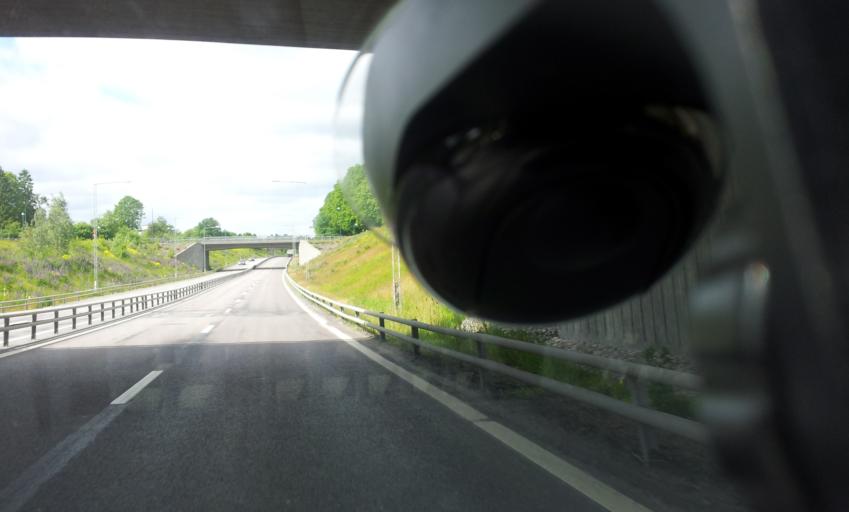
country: SE
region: OEstergoetland
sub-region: Norrkopings Kommun
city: Norrkoping
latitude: 58.5773
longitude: 16.2024
